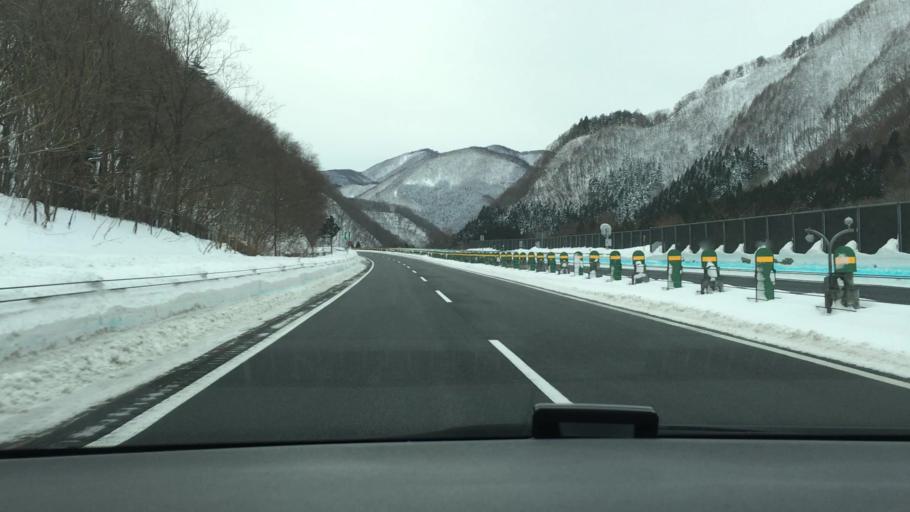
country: JP
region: Akita
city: Hanawa
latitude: 40.1259
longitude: 140.9098
